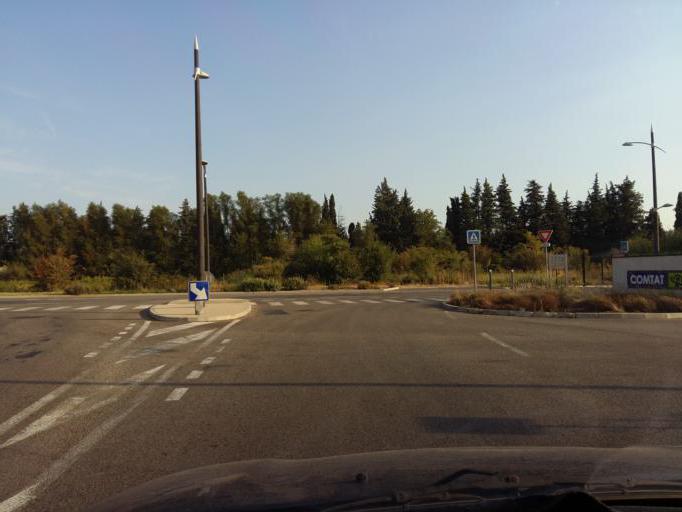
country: FR
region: Provence-Alpes-Cote d'Azur
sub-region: Departement du Vaucluse
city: Monteux
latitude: 44.0295
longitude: 4.9758
